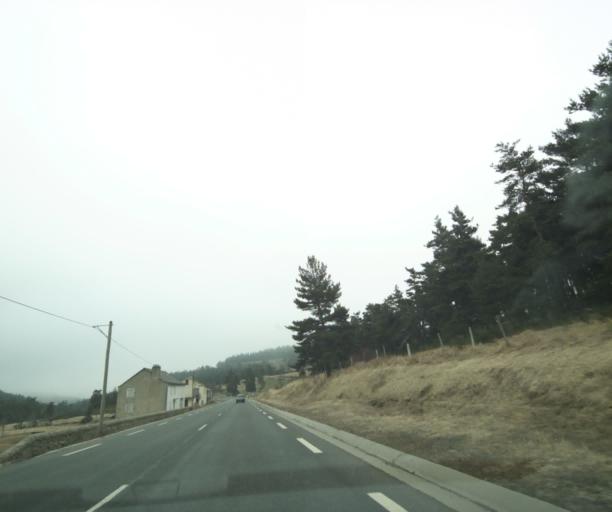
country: FR
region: Languedoc-Roussillon
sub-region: Departement de la Lozere
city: Langogne
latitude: 44.6637
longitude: 3.7592
